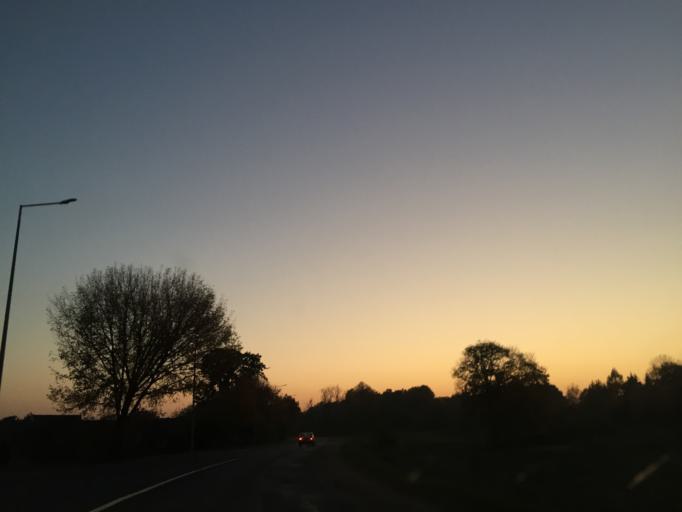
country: LT
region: Klaipedos apskritis
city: Kretinga
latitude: 55.9018
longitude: 21.2434
